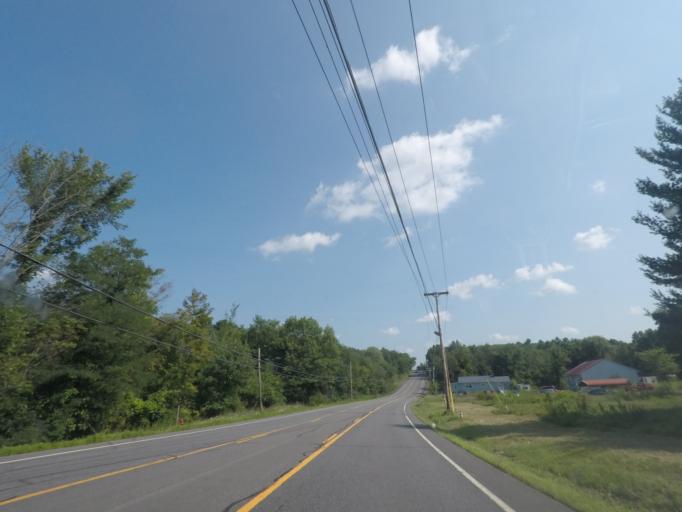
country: US
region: New York
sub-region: Rensselaer County
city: Nassau
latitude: 42.5371
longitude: -73.6613
